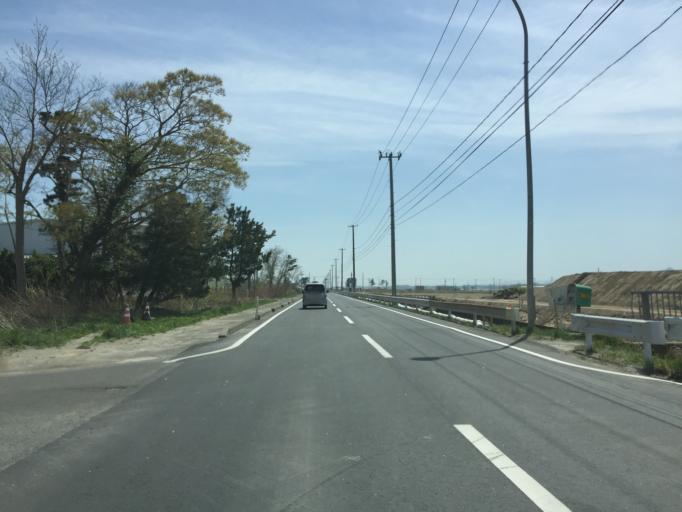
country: JP
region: Miyagi
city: Watari
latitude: 37.9638
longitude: 140.9082
